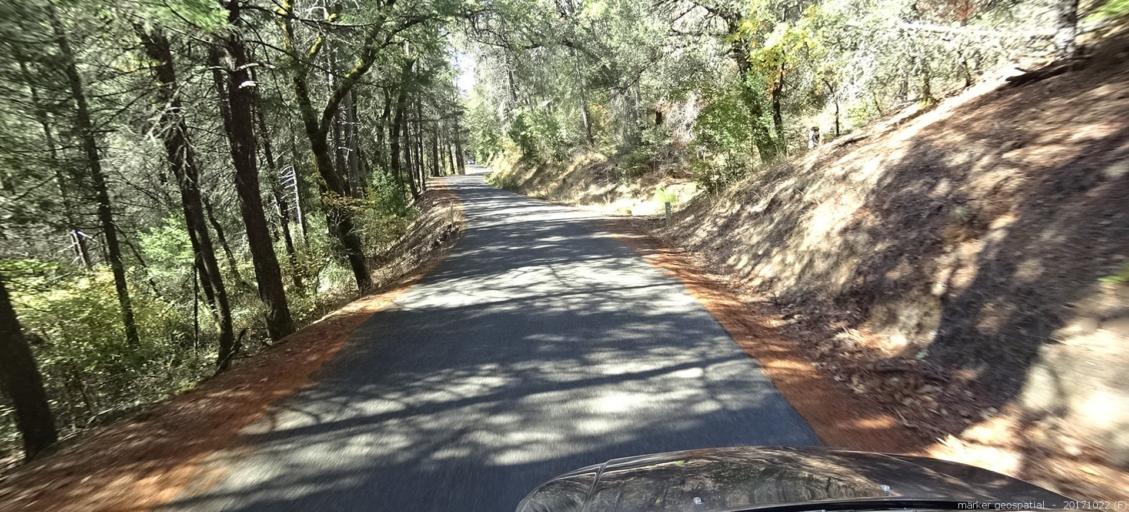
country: US
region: California
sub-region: Shasta County
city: Central Valley (historical)
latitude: 40.9327
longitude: -122.4644
